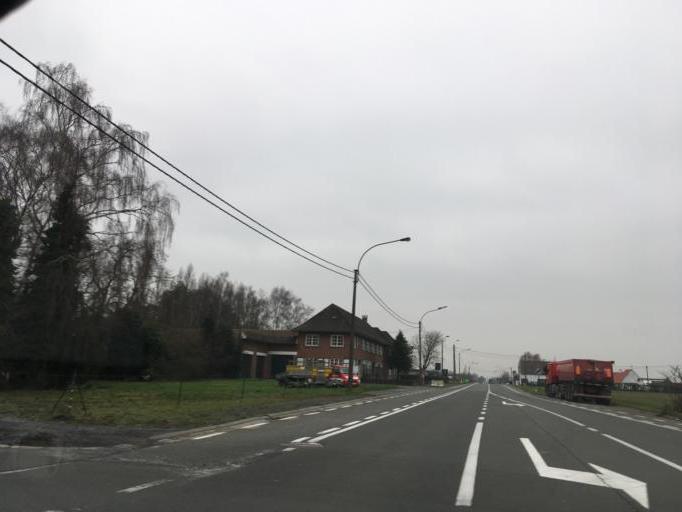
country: BE
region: Flanders
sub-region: Provincie West-Vlaanderen
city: Pittem
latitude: 50.9651
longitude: 3.2438
